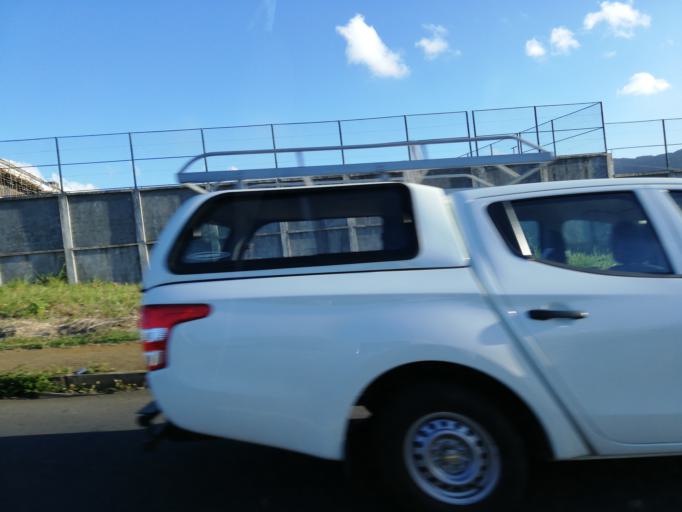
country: MU
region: Plaines Wilhems
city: Ebene
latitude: -20.2393
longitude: 57.4825
